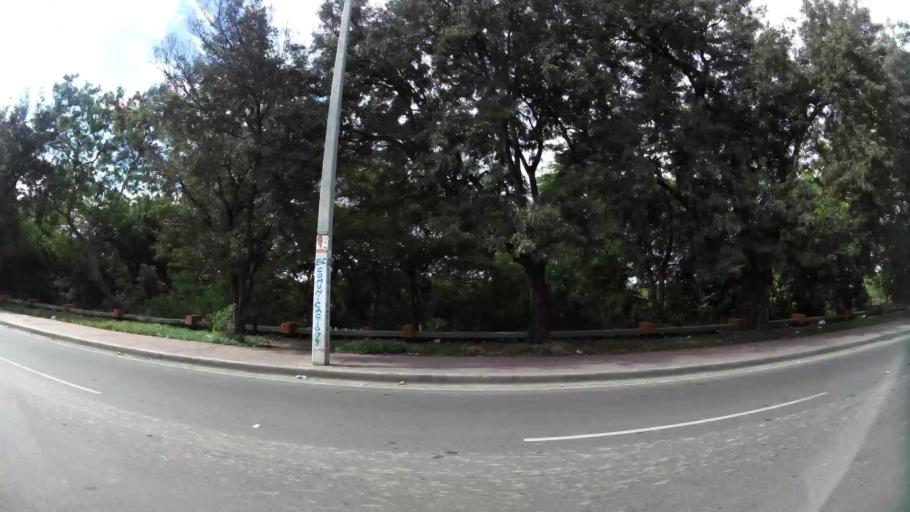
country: DO
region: Santiago
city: Santiago de los Caballeros
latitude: 19.4715
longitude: -70.7179
